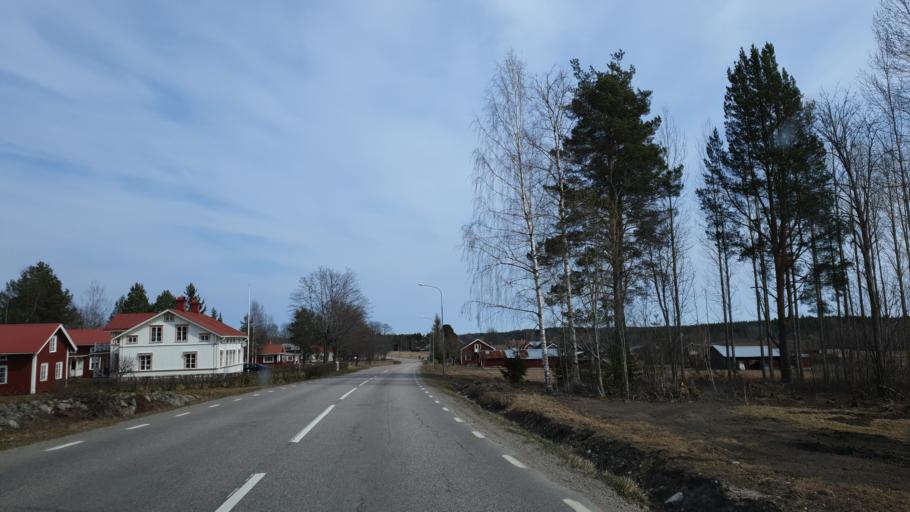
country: SE
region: Gaevleborg
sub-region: Gavle Kommun
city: Norrsundet
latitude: 61.0005
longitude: 17.1118
